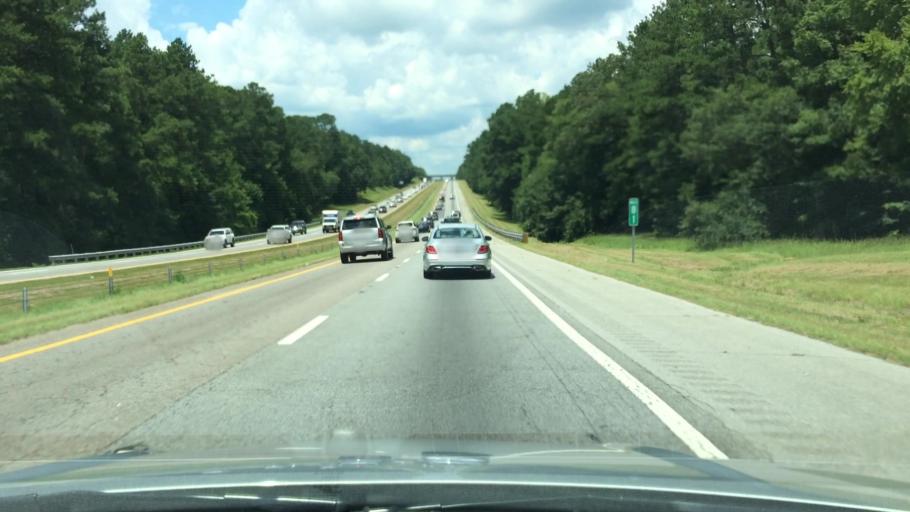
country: US
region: South Carolina
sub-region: Newberry County
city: Prosperity
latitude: 34.2473
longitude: -81.4787
